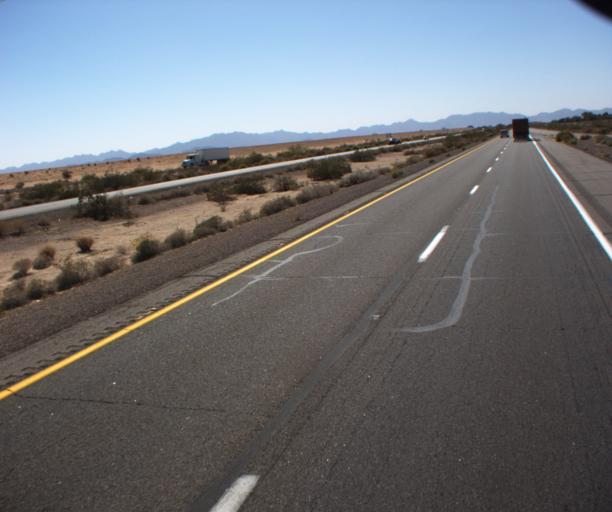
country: US
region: Arizona
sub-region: Yuma County
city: Wellton
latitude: 32.6813
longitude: -114.0240
